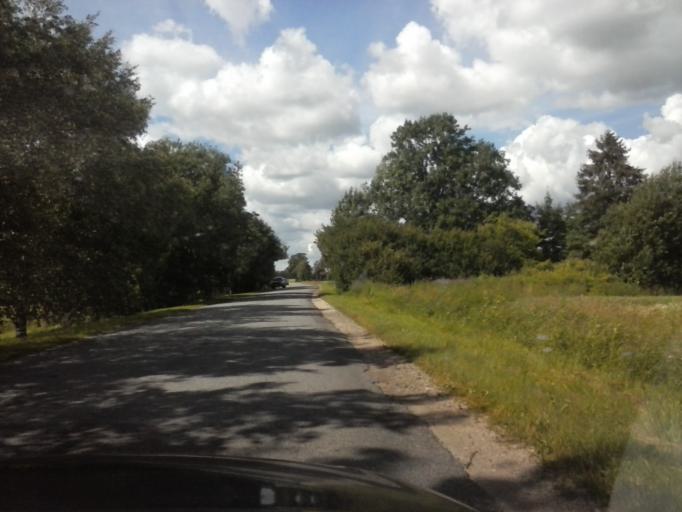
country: EE
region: Laeaene-Virumaa
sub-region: Vaeike-Maarja vald
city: Vaike-Maarja
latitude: 59.0575
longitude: 26.3399
